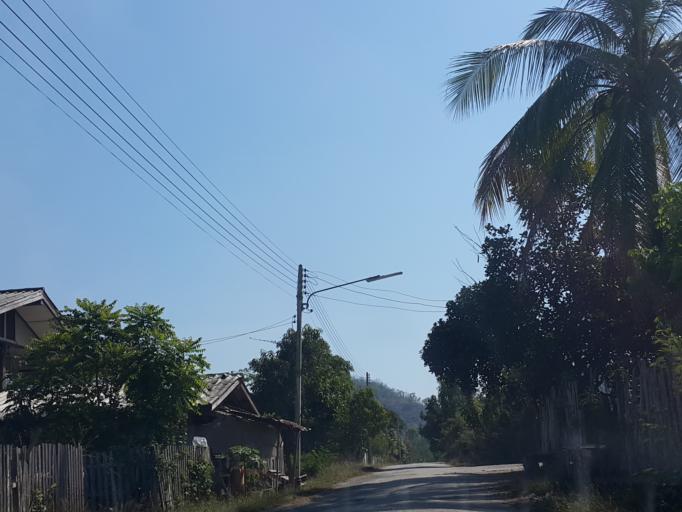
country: TH
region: Sukhothai
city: Thung Saliam
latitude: 17.3428
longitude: 99.4441
